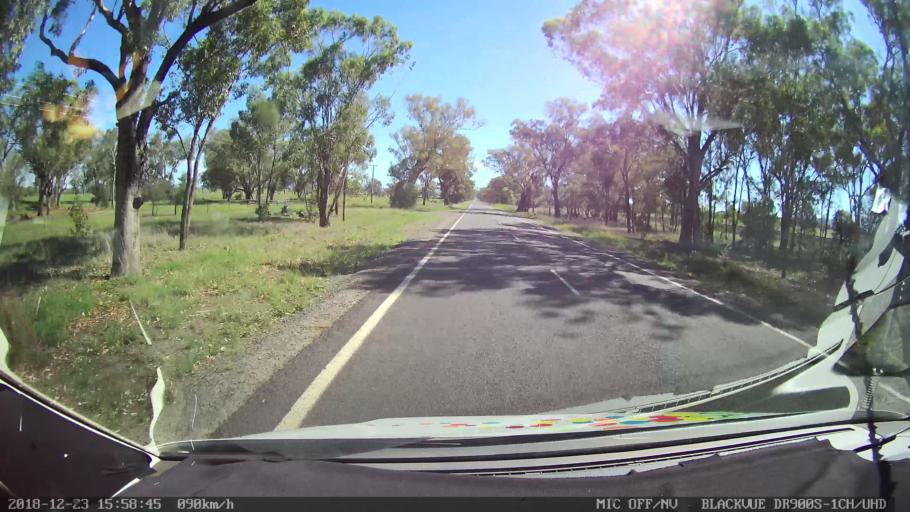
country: AU
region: New South Wales
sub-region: Tamworth Municipality
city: Phillip
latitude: -31.1918
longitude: 150.8391
